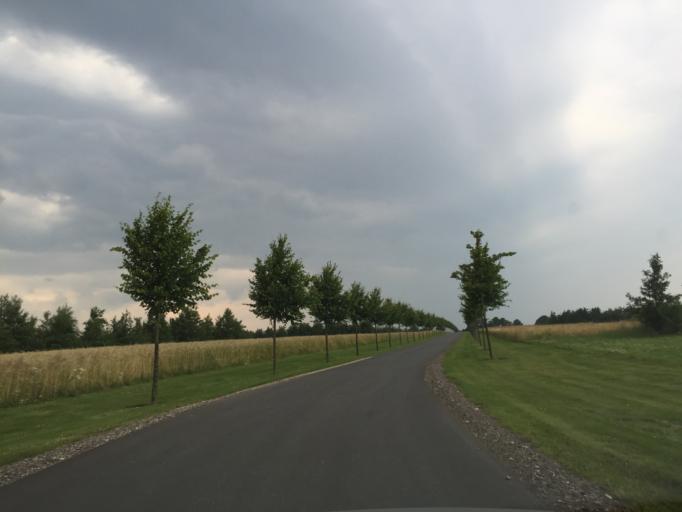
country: DK
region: Central Jutland
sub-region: Viborg Kommune
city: Bjerringbro
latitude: 56.3307
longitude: 9.6433
